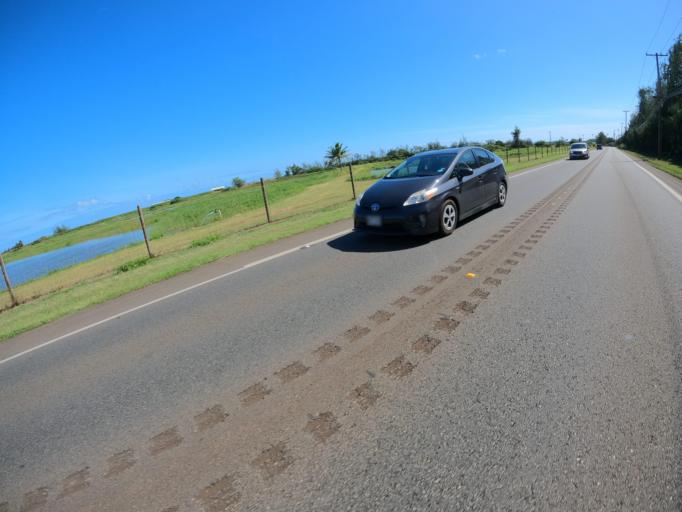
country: US
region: Hawaii
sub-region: Honolulu County
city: Kahuku
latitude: 21.6819
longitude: -157.9582
